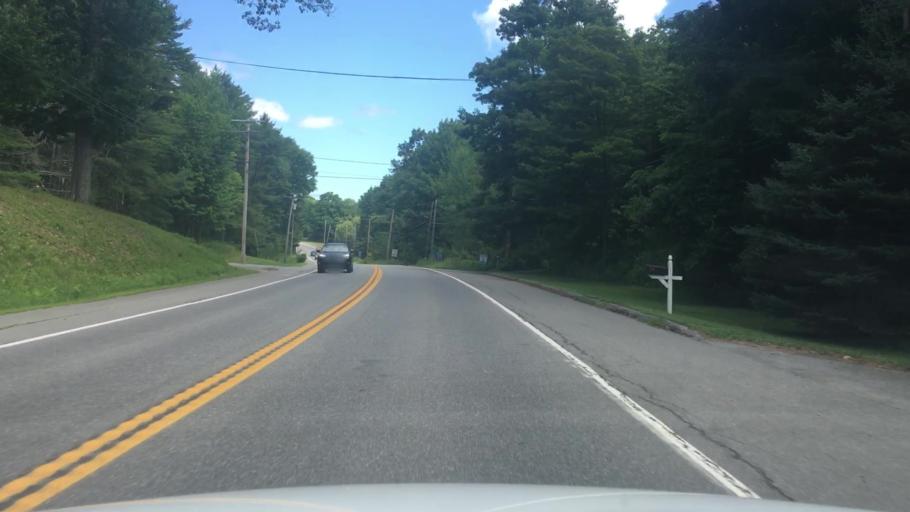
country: US
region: Maine
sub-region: Waldo County
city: Belfast
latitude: 44.3949
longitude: -68.9885
